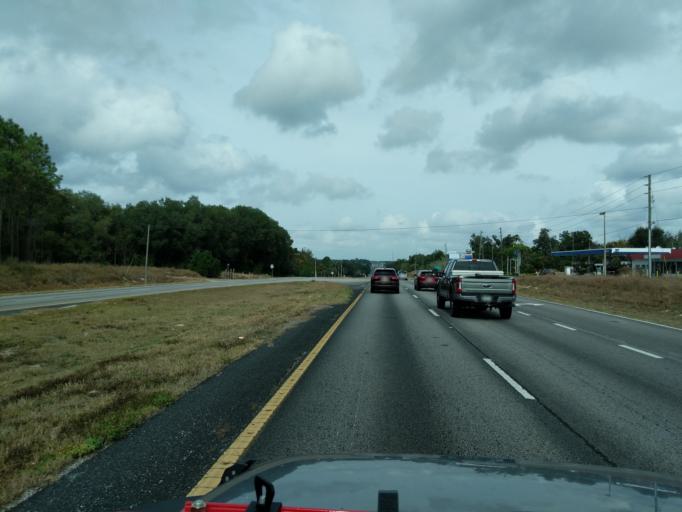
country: US
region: Florida
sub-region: Orange County
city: Tangerine
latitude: 28.7736
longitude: -81.6242
